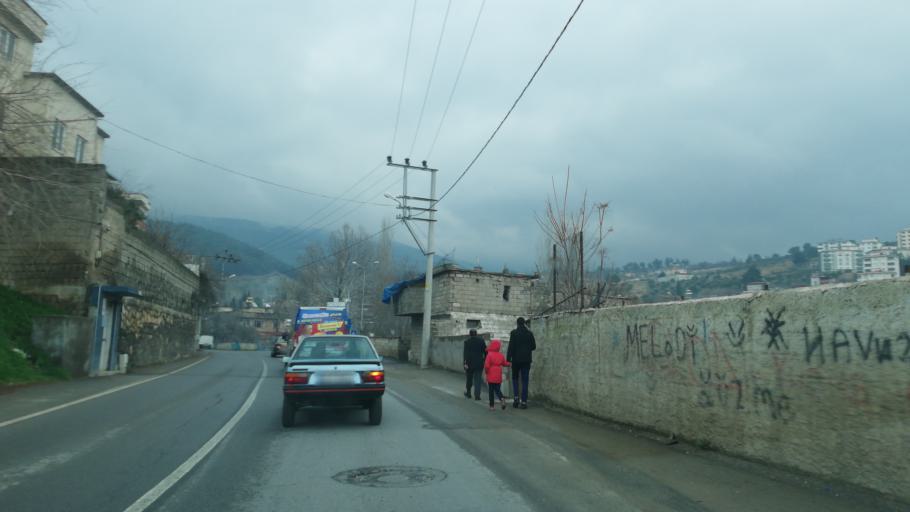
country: TR
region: Kahramanmaras
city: Kahramanmaras
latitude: 37.5941
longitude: 36.9353
